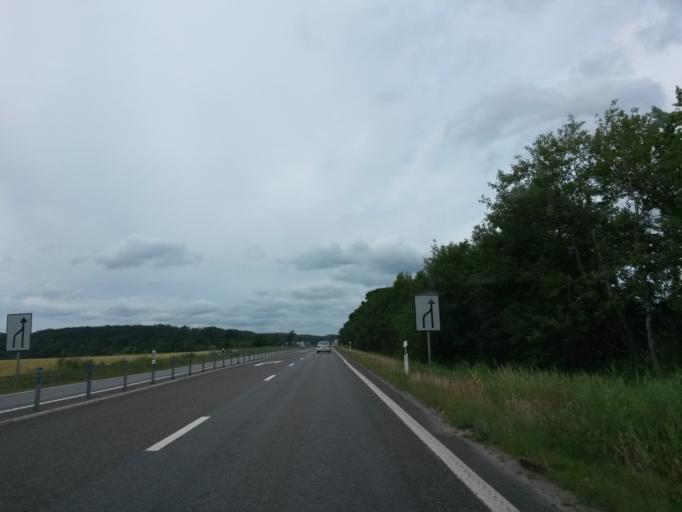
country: SE
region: Halland
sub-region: Varbergs Kommun
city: Varberg
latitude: 57.1547
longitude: 12.2704
